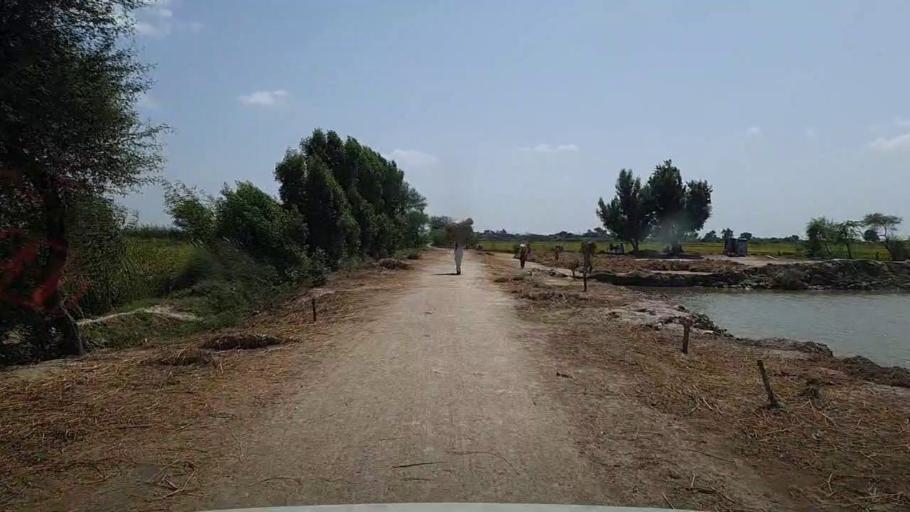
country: PK
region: Sindh
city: Kario
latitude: 24.6384
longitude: 68.5719
